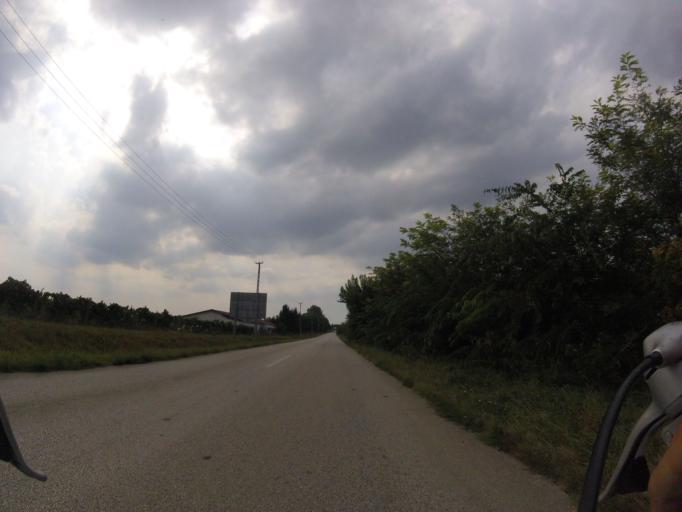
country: HU
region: Szabolcs-Szatmar-Bereg
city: Nyirpazony
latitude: 48.0120
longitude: 21.8378
